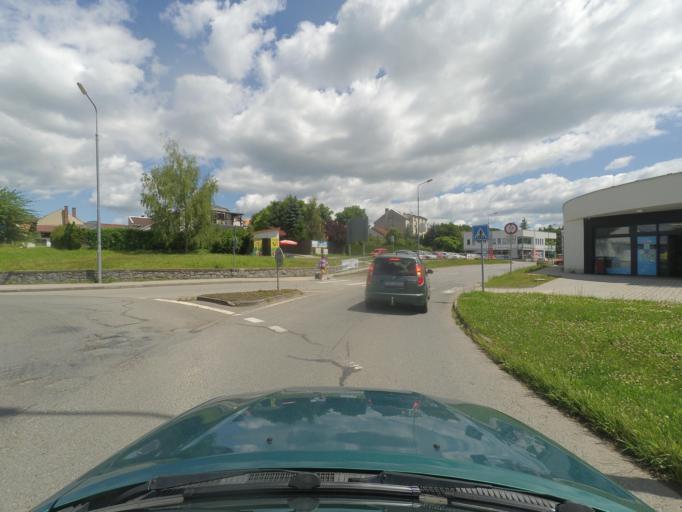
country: CZ
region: Pardubicky
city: Zamberk
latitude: 50.0847
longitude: 16.4617
